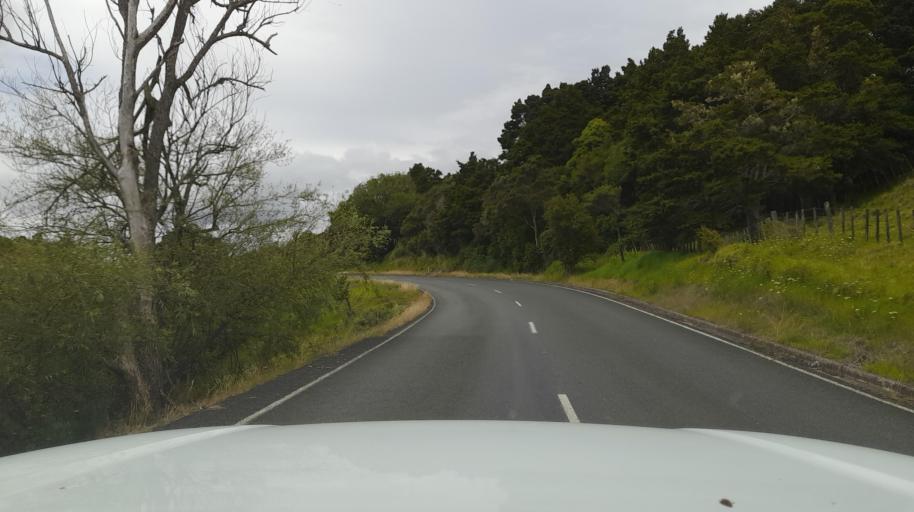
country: NZ
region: Northland
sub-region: Far North District
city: Kaitaia
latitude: -35.3569
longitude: 173.4891
